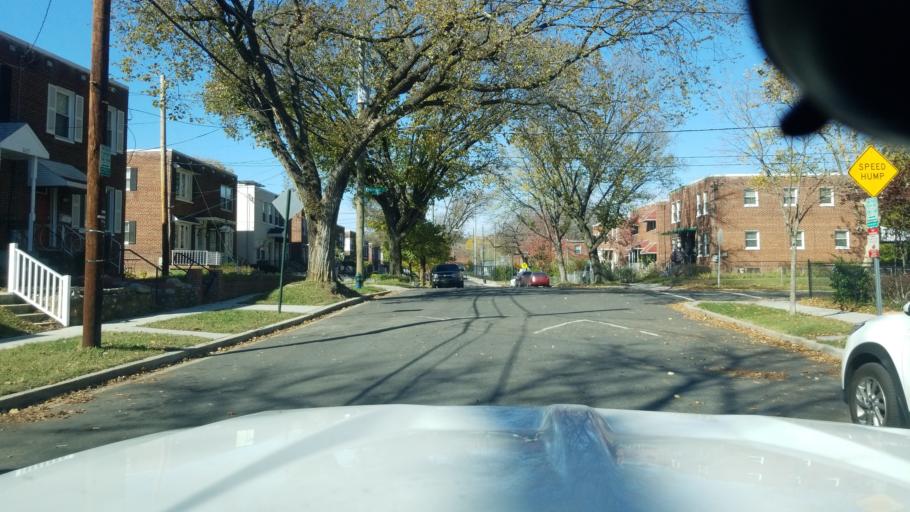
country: US
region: Maryland
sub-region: Prince George's County
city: Chillum
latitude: 38.9576
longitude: -76.9977
